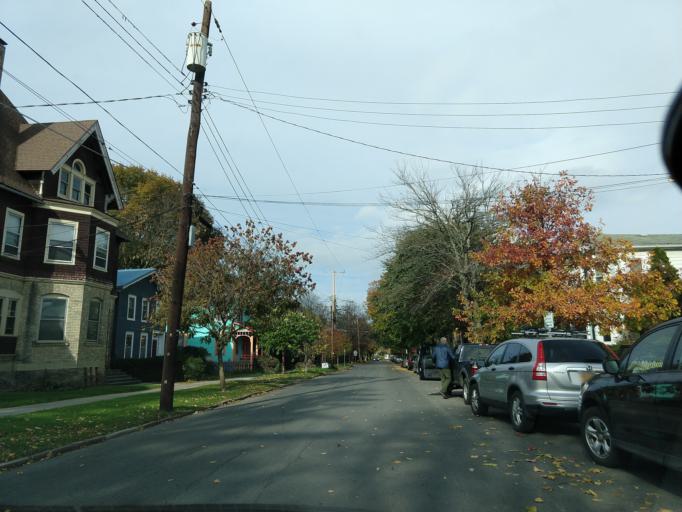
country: US
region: New York
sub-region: Tompkins County
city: Ithaca
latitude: 42.4417
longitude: -76.5009
